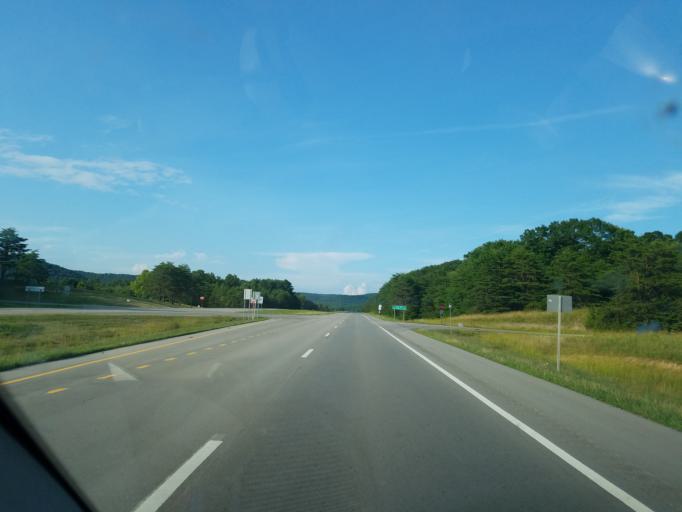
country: US
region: Ohio
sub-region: Adams County
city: Peebles
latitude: 38.9823
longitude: -83.3252
